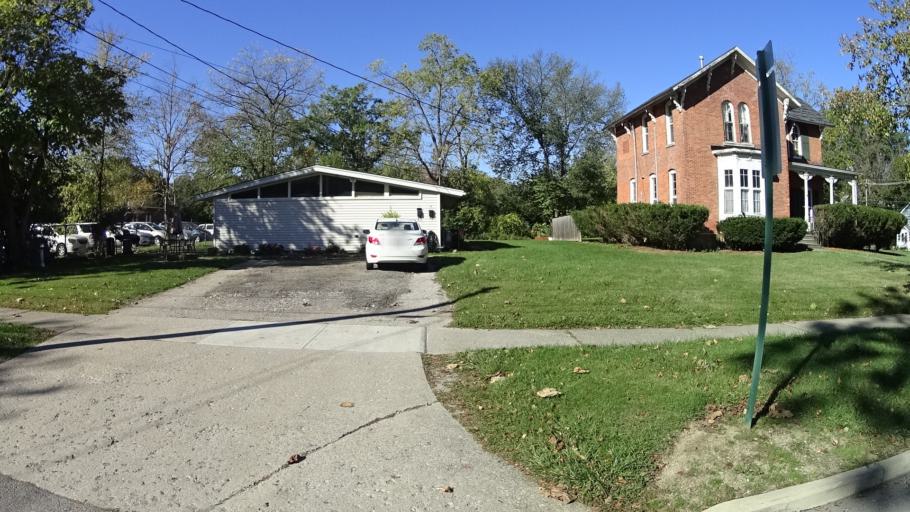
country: US
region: Ohio
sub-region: Lorain County
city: Oberlin
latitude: 41.2915
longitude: -82.2284
